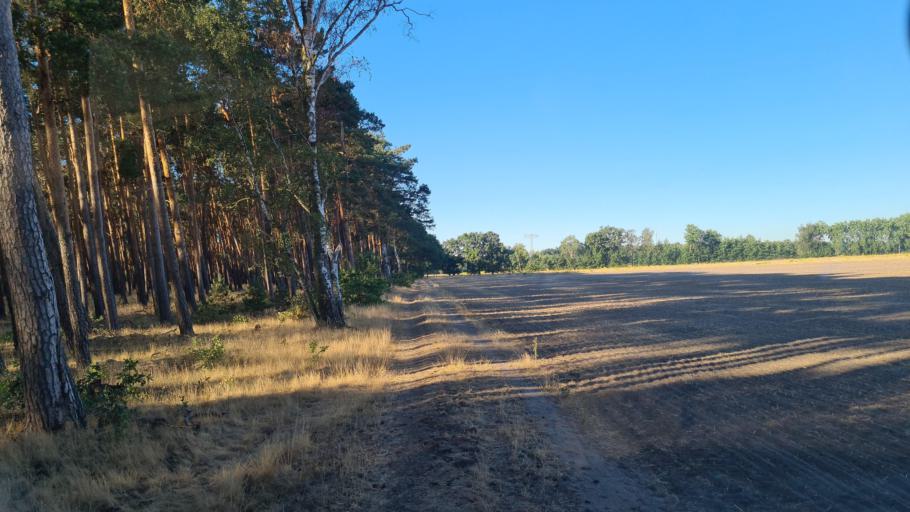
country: DE
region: Brandenburg
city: Doberlug-Kirchhain
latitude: 51.6380
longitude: 13.5930
